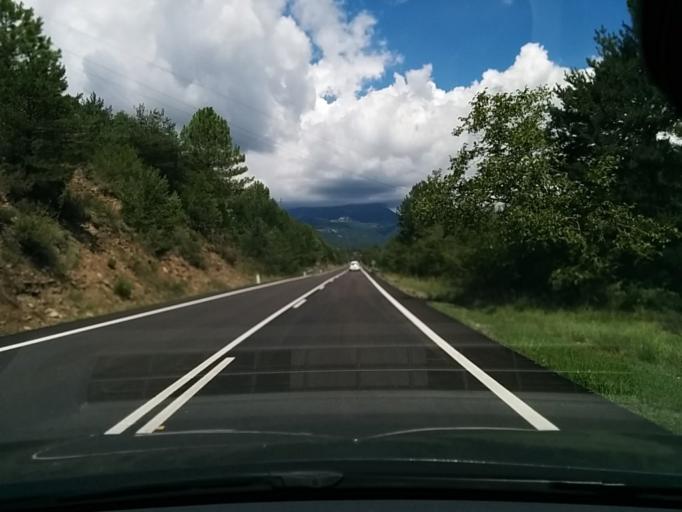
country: ES
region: Aragon
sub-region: Provincia de Huesca
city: Laspuna
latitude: 42.4868
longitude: 0.1476
